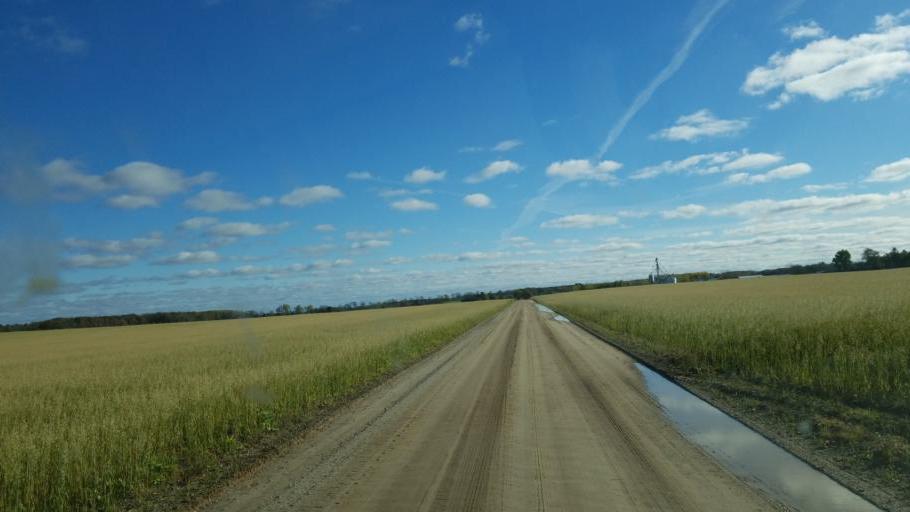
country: US
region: Michigan
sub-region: Montcalm County
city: Edmore
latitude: 43.4663
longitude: -85.0320
